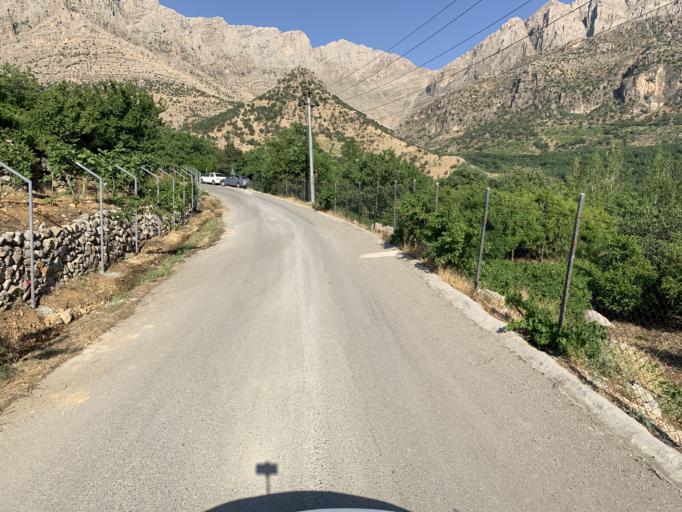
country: IQ
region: As Sulaymaniyah
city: Qeladize
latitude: 35.9917
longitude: 45.1974
